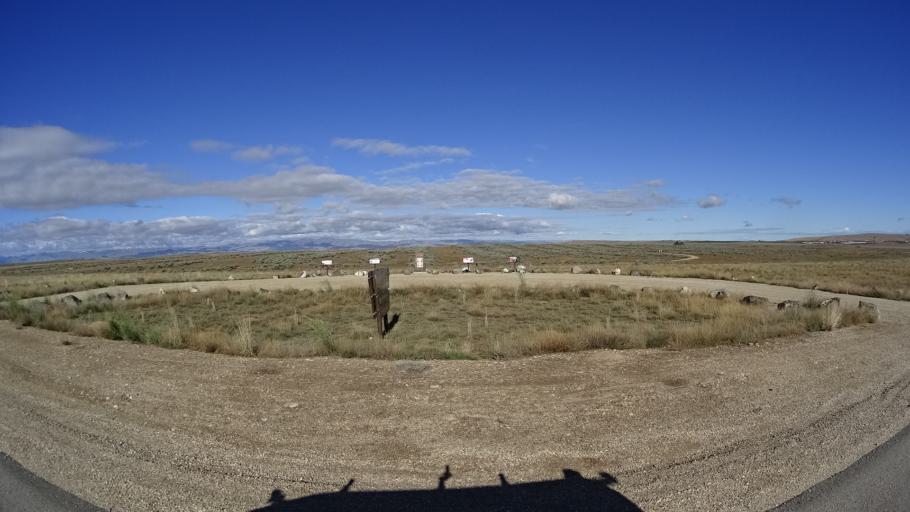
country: US
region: Idaho
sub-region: Ada County
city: Kuna
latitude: 43.3926
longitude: -116.4139
